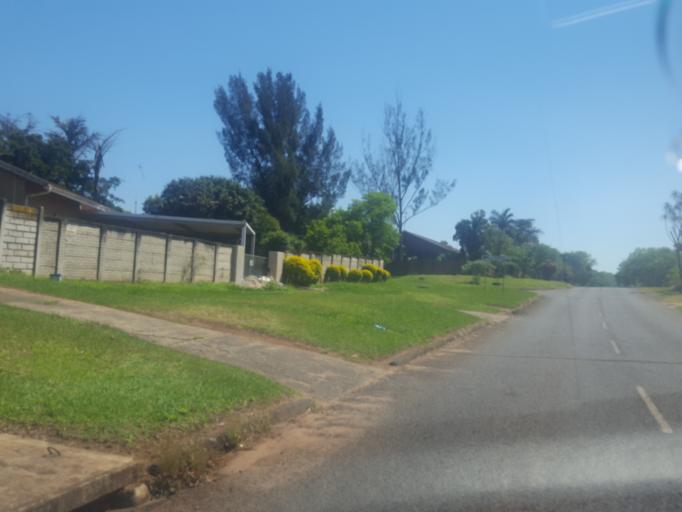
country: ZA
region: KwaZulu-Natal
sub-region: uThungulu District Municipality
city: Empangeni
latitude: -28.7588
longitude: 31.9051
